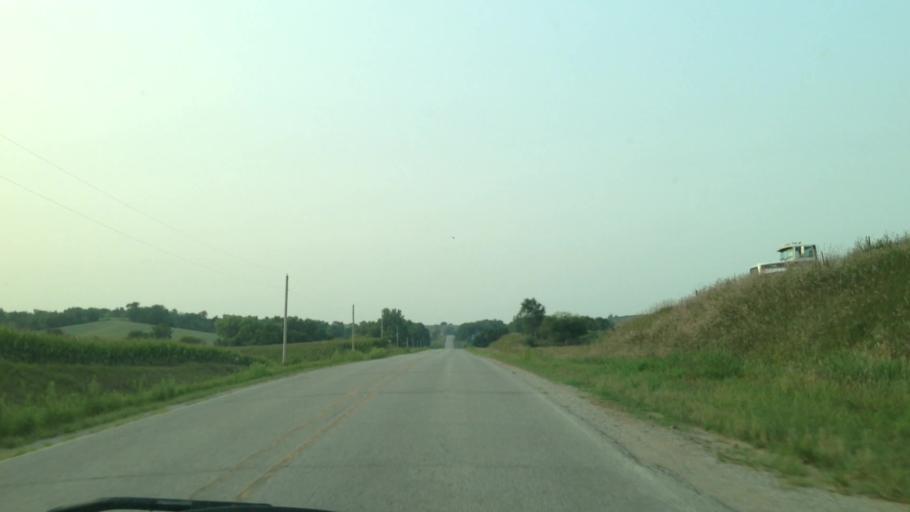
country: US
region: Iowa
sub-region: Iowa County
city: Marengo
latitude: 41.8681
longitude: -92.0888
